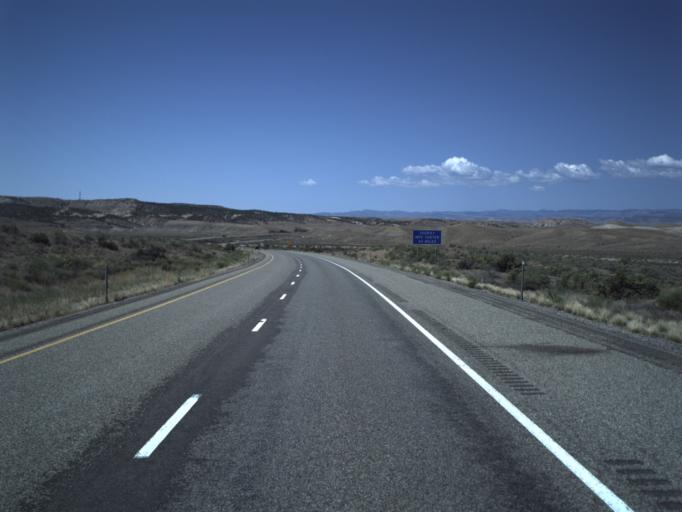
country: US
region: Colorado
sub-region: Mesa County
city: Loma
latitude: 39.1949
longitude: -109.0662
